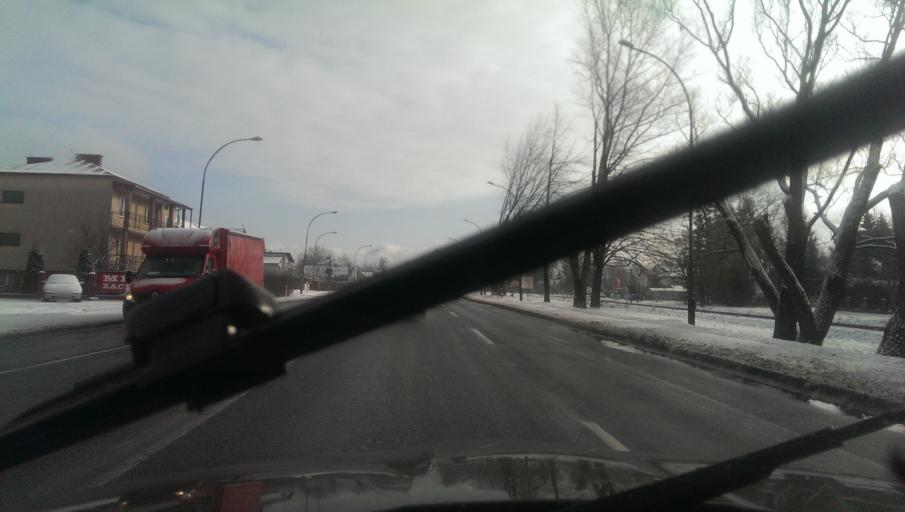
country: PL
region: Subcarpathian Voivodeship
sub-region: Powiat sanocki
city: Sanok
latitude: 49.5669
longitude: 22.1721
